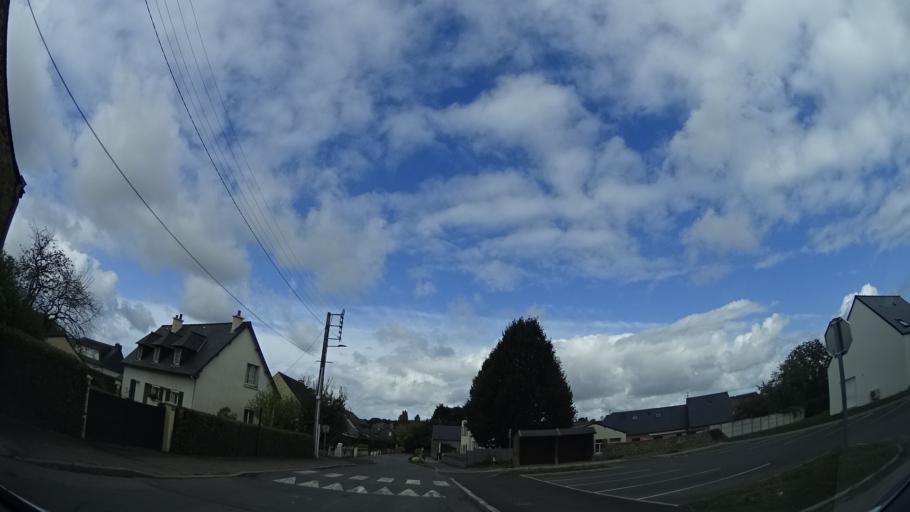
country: FR
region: Brittany
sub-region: Departement d'Ille-et-Vilaine
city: Montreuil-sur-Ille
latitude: 48.3057
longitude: -1.6666
